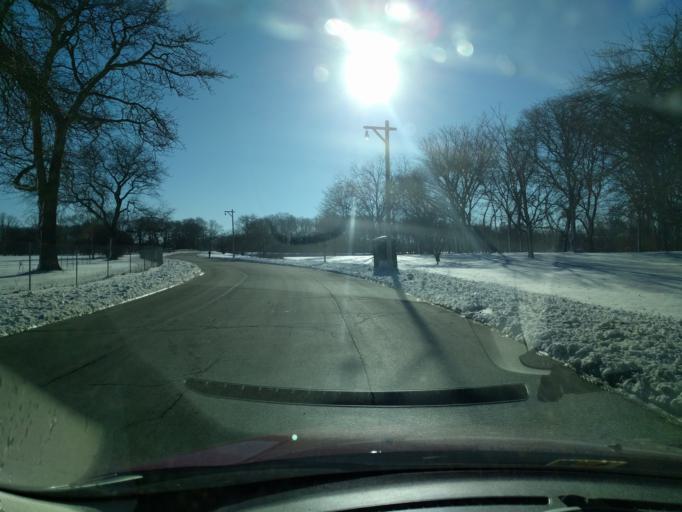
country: US
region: Wisconsin
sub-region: Milwaukee County
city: Glendale
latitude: 43.1089
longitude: -87.9275
